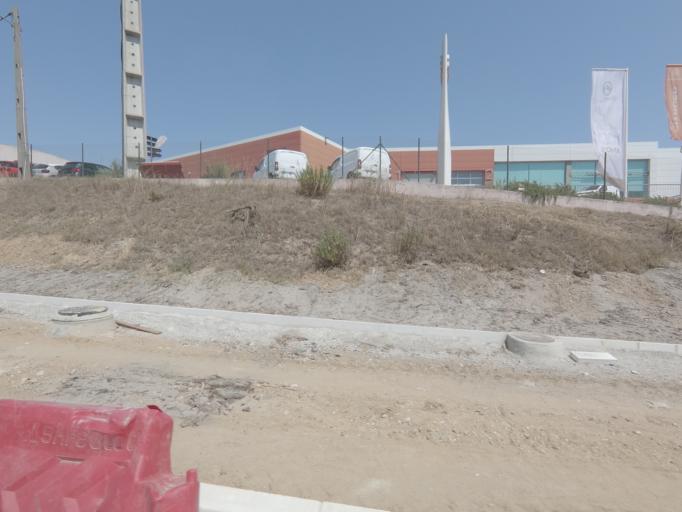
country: PT
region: Setubal
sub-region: Palmela
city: Palmela
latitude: 38.5496
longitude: -8.8859
